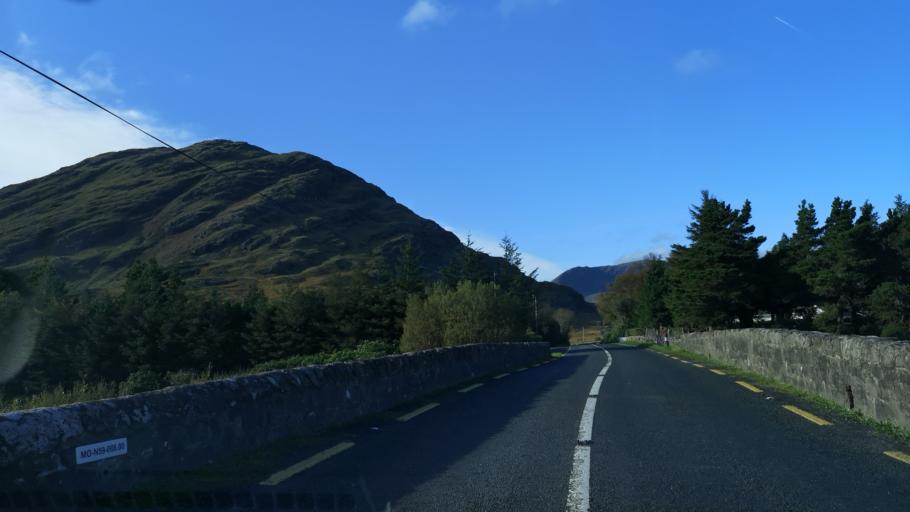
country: IE
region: Connaught
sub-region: Maigh Eo
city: Westport
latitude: 53.6300
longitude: -9.6106
